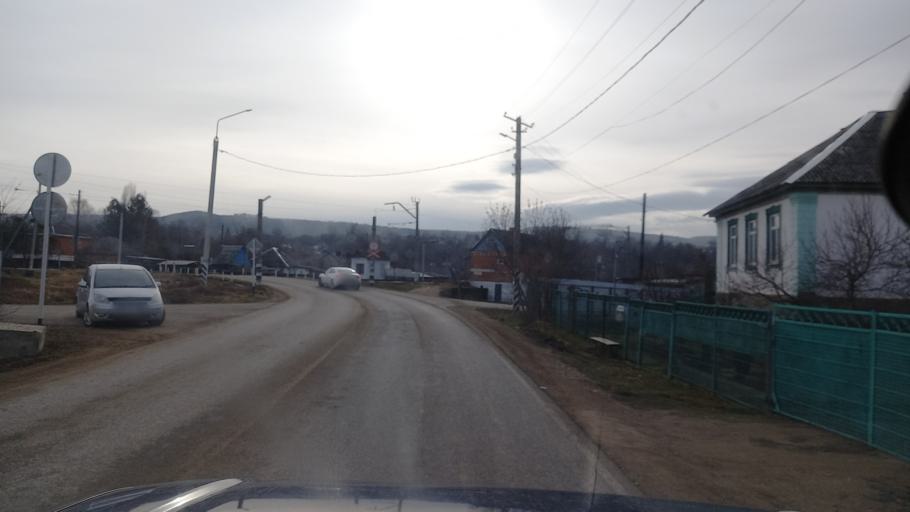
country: RU
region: Adygeya
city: Kamennomostskiy
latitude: 44.2974
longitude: 40.1881
